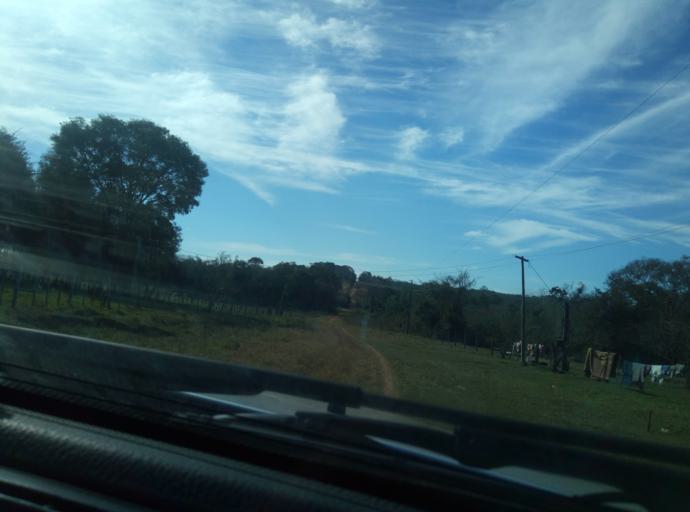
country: PY
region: Caaguazu
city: Carayao
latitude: -25.1682
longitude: -56.2930
